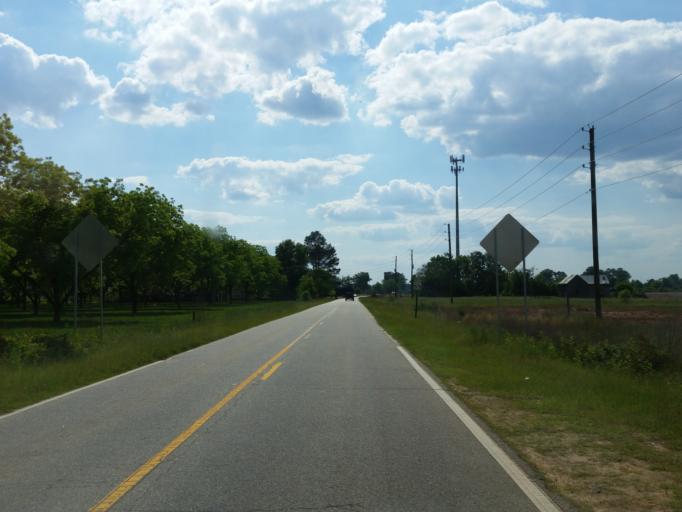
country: US
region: Georgia
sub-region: Houston County
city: Centerville
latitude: 32.5783
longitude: -83.7203
